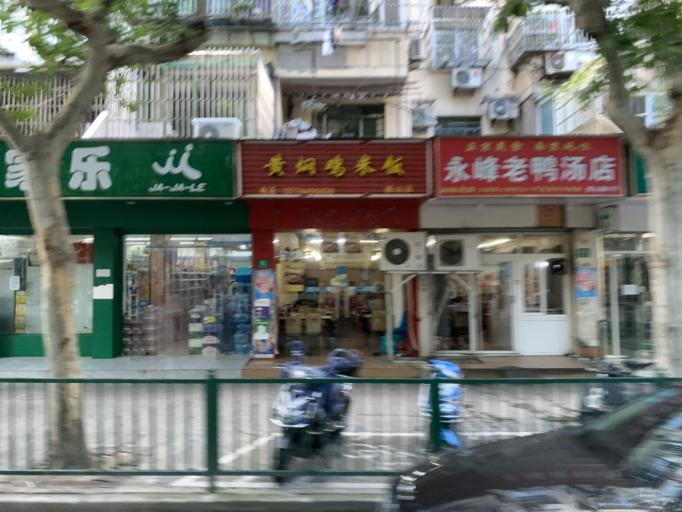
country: CN
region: Shanghai Shi
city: Pudong
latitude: 31.2448
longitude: 121.5385
